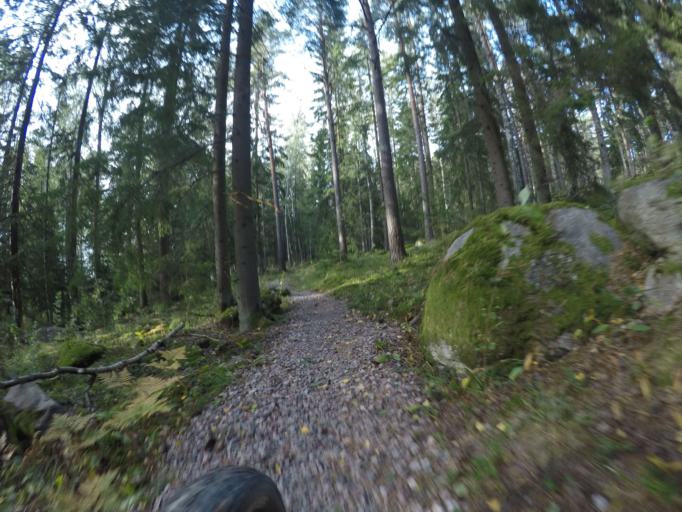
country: SE
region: Vaestmanland
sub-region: Kopings Kommun
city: Koping
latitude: 59.5292
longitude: 15.9978
